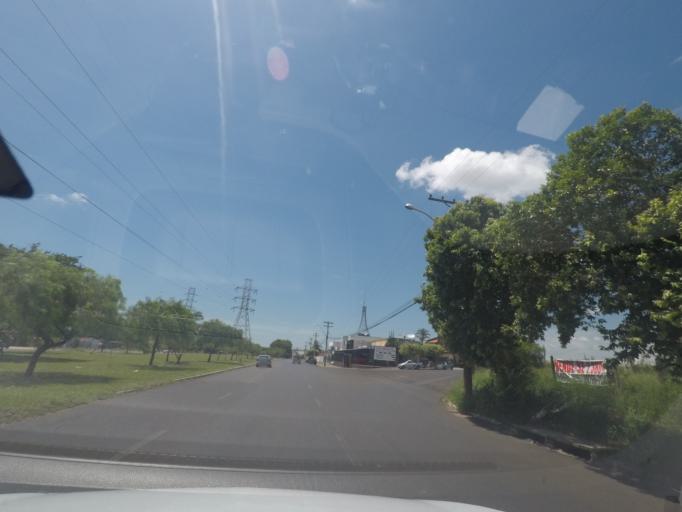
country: BR
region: Sao Paulo
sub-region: Matao
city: Matao
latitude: -21.6157
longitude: -48.3664
